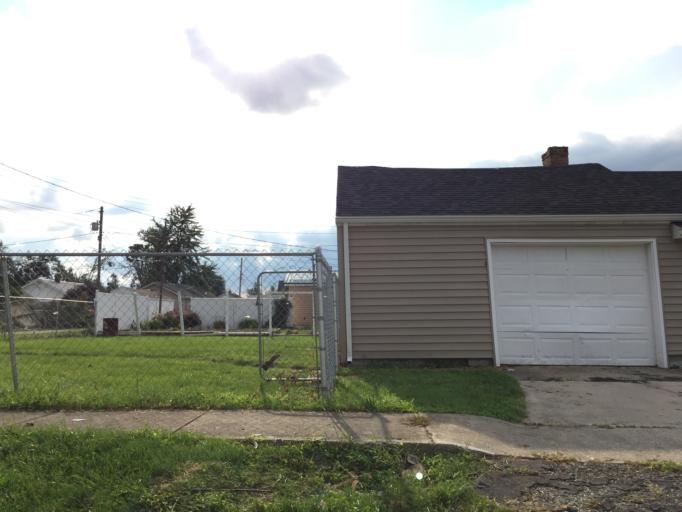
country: US
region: Indiana
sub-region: Howard County
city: Kokomo
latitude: 40.4669
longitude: -86.1258
